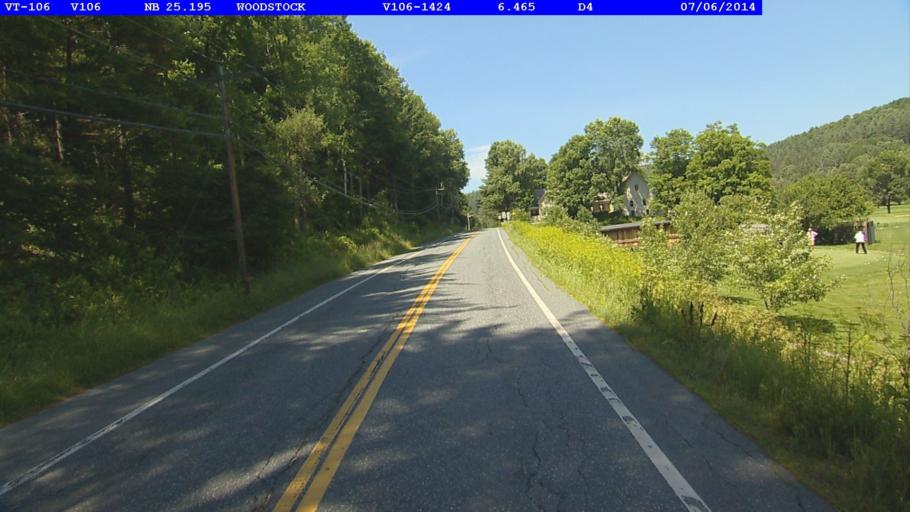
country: US
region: Vermont
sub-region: Windsor County
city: Woodstock
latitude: 43.6133
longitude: -72.5173
